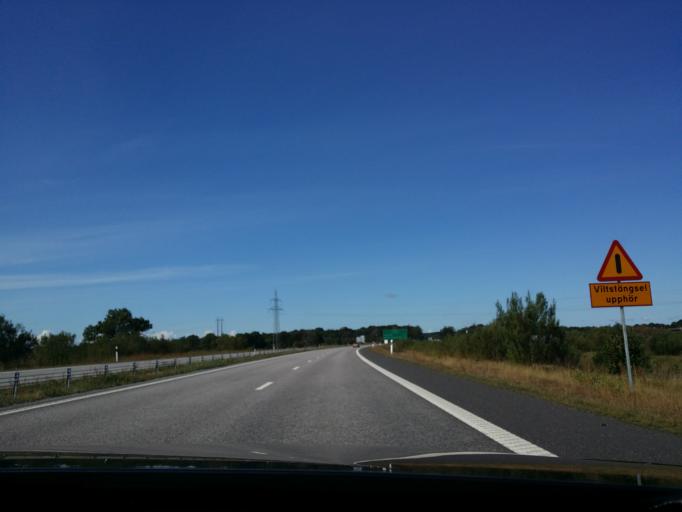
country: SE
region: Skane
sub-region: Bromolla Kommun
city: Bromoella
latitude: 56.0619
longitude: 14.4909
